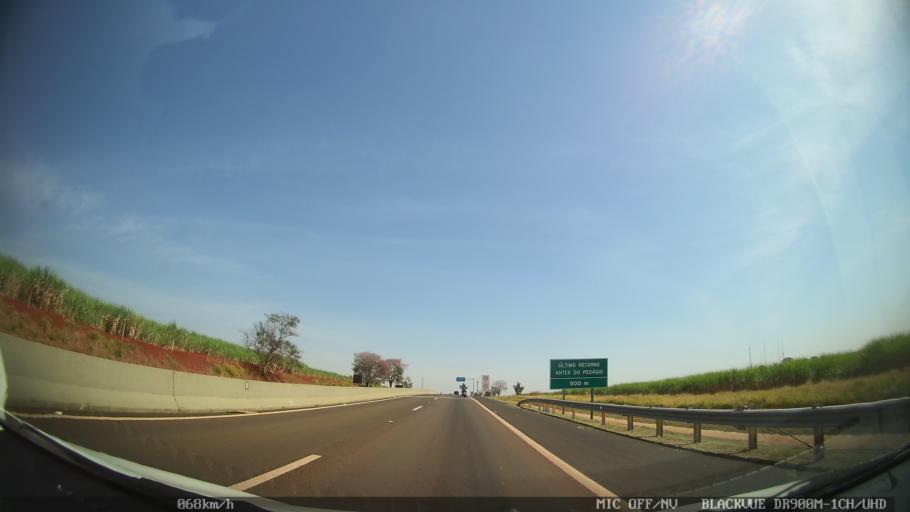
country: BR
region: Sao Paulo
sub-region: Ribeirao Preto
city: Ribeirao Preto
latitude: -21.1662
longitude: -47.8907
